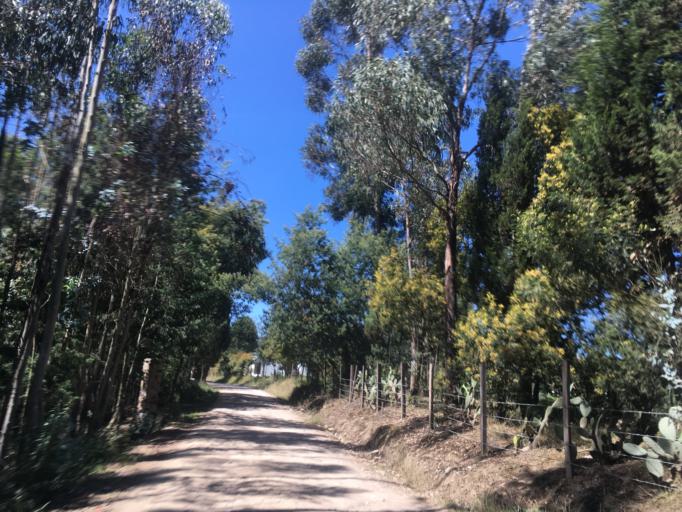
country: CO
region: Boyaca
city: Tuta
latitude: 5.6705
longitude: -73.2773
